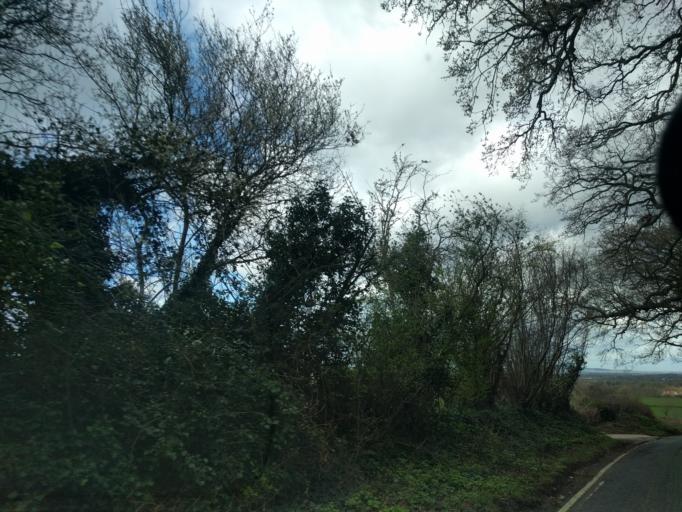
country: GB
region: England
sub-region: Gloucestershire
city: Stonehouse
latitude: 51.7167
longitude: -2.3030
